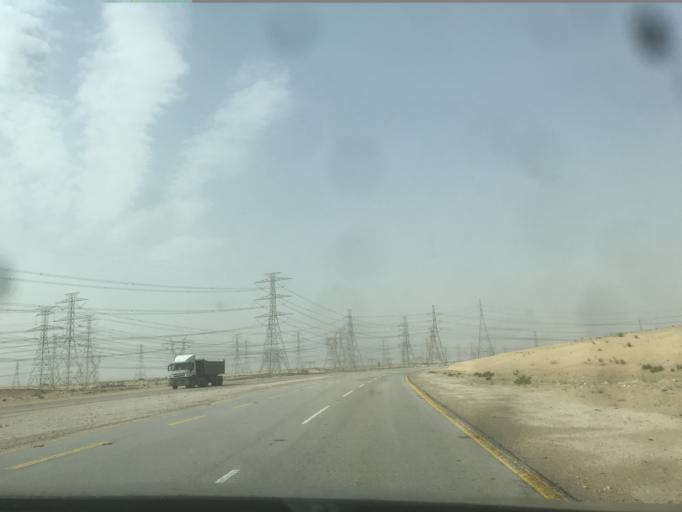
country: SA
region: Eastern Province
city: Abqaiq
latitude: 25.9066
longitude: 49.9179
